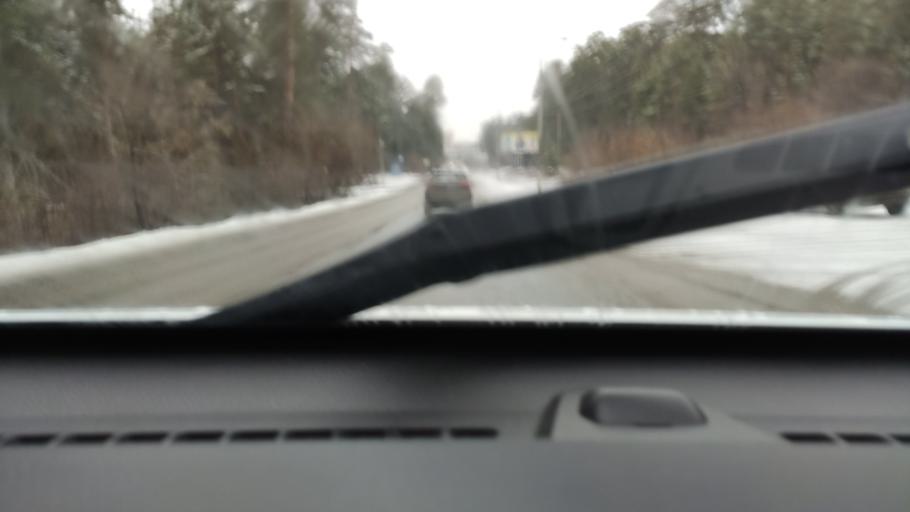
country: RU
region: Samara
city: Tol'yatti
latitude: 53.4777
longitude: 49.3450
